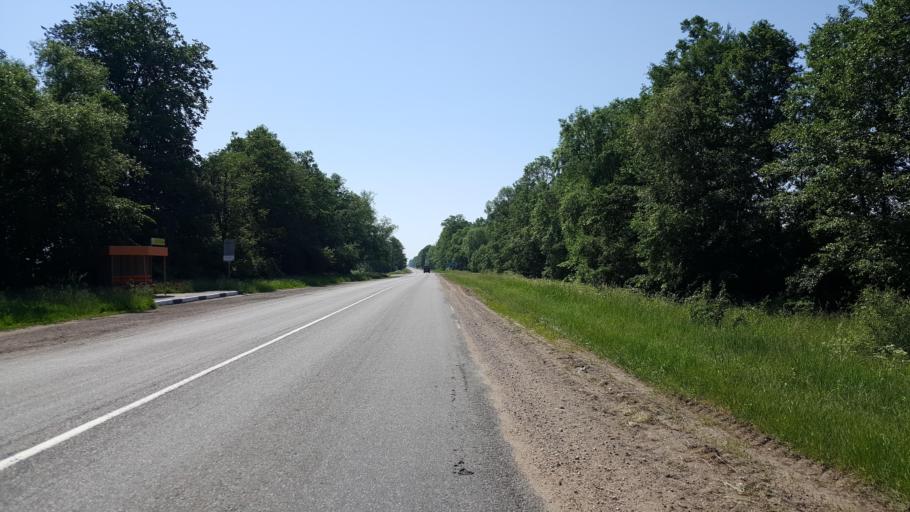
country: BY
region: Brest
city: Zhabinka
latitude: 52.2390
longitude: 23.9782
